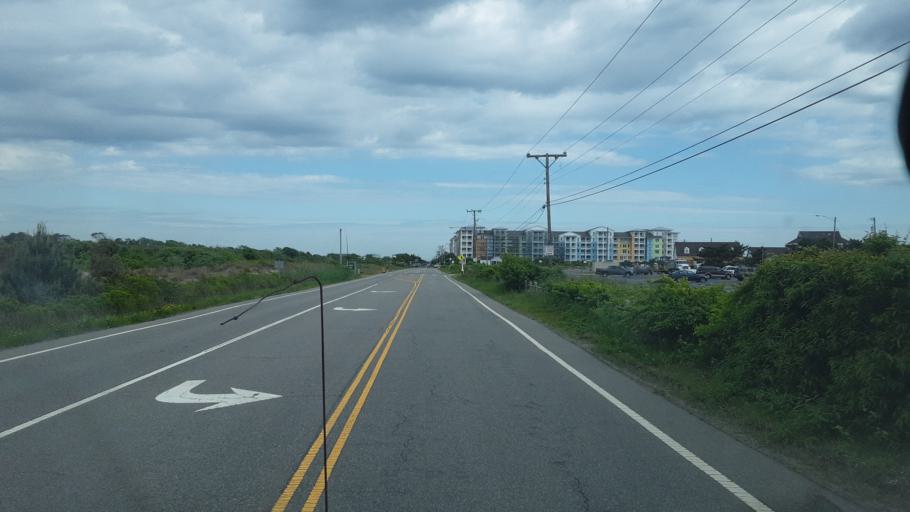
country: US
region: Virginia
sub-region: City of Virginia Beach
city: Virginia Beach
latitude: 36.6923
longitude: -75.9247
